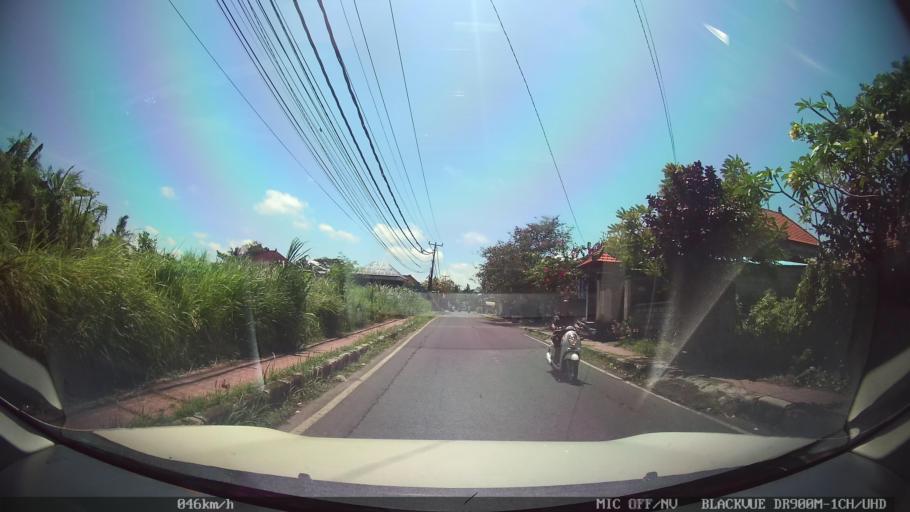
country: ID
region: Bali
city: Klungkung
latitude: -8.5712
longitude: 115.3485
